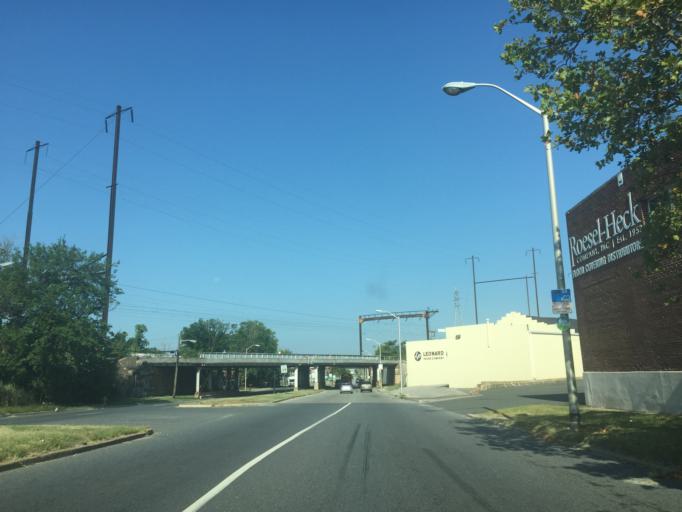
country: US
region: Maryland
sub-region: Baltimore County
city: Rosedale
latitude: 39.2998
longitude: -76.5608
